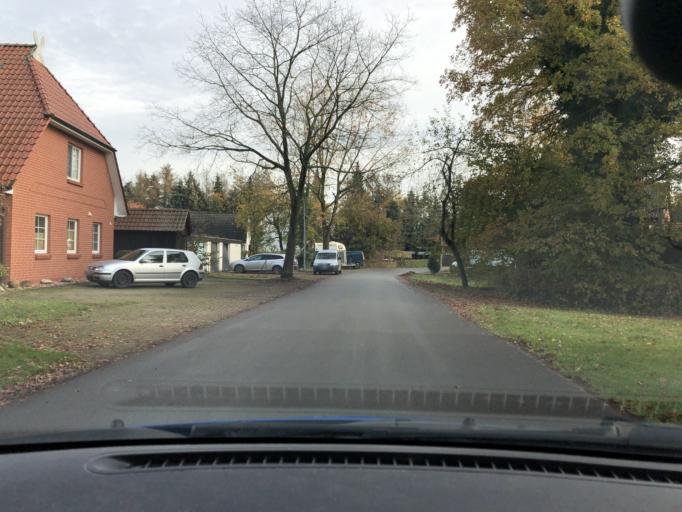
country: DE
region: Lower Saxony
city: Brietlingen
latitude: 53.3528
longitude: 10.4438
